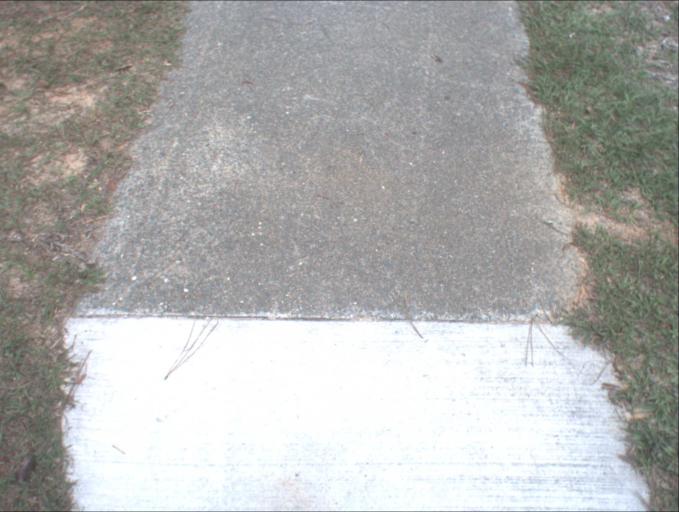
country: AU
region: Queensland
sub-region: Logan
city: Park Ridge South
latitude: -27.7020
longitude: 153.0388
